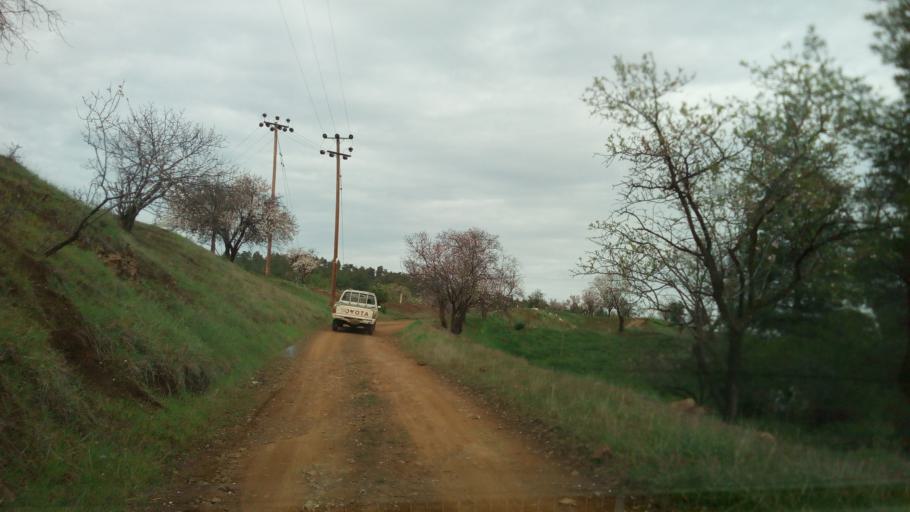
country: CY
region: Lefkosia
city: Klirou
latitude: 34.9975
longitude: 33.1069
